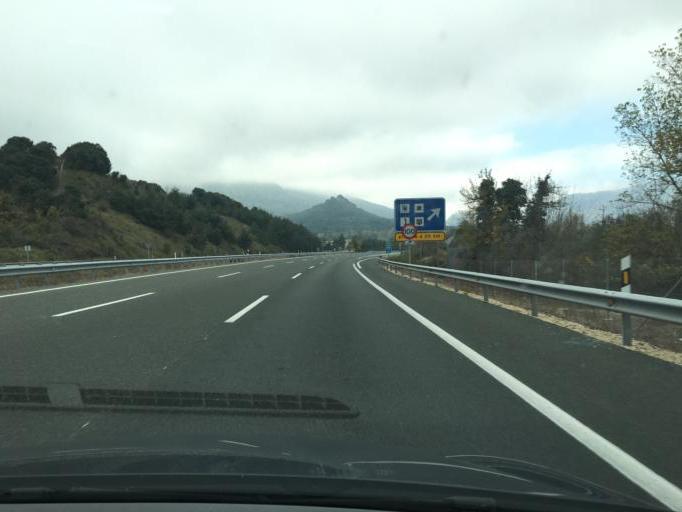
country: ES
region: Castille and Leon
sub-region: Provincia de Burgos
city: Ameyugo
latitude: 42.6529
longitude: -3.0635
